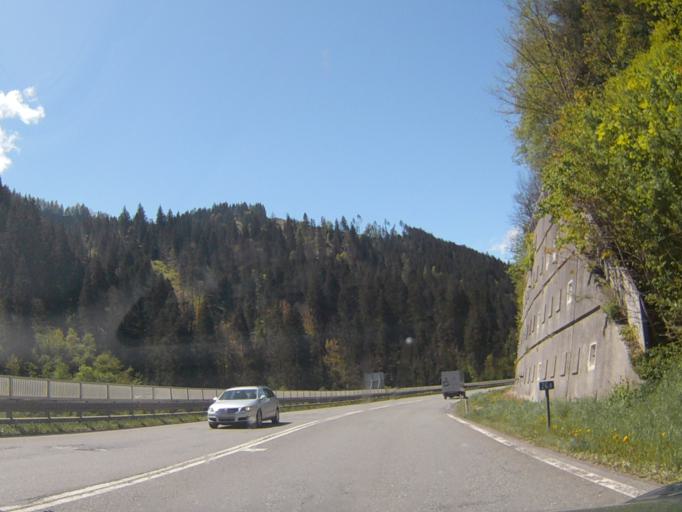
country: AT
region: Salzburg
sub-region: Politischer Bezirk Zell am See
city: Taxenbach
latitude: 47.3049
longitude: 13.0048
